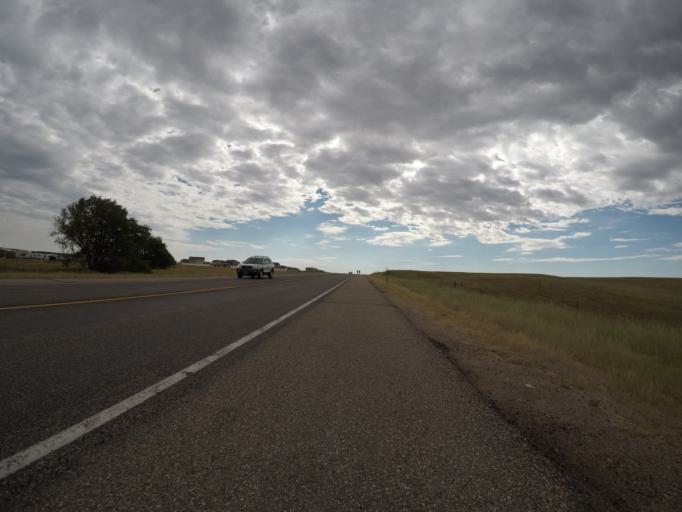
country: US
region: Wyoming
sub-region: Laramie County
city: Cheyenne
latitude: 41.1315
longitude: -104.8675
